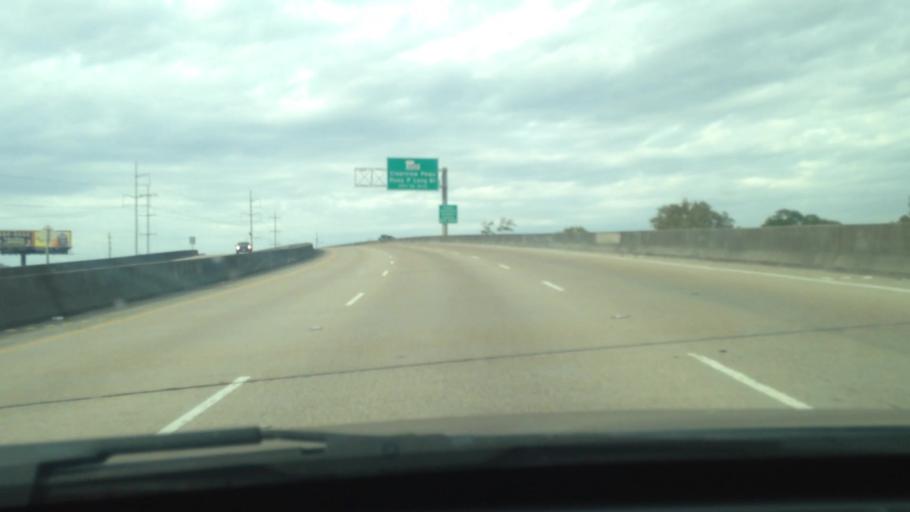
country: US
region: Louisiana
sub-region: Jefferson Parish
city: Metairie Terrace
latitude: 29.9717
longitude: -90.1706
